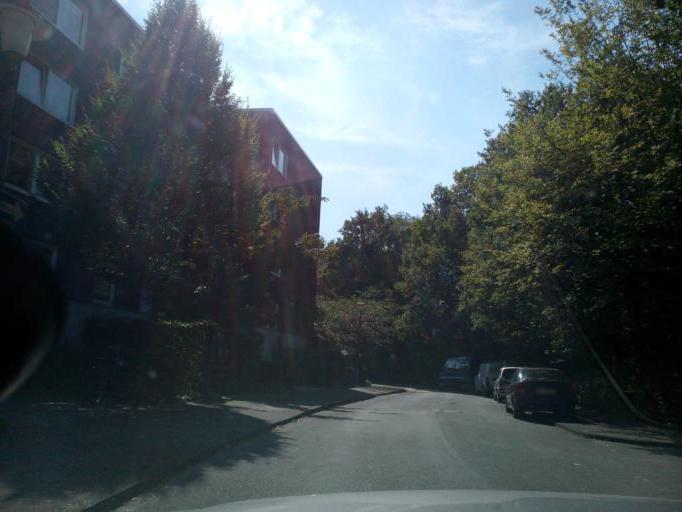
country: DE
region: North Rhine-Westphalia
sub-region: Regierungsbezirk Munster
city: Muenster
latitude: 51.9267
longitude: 7.6164
